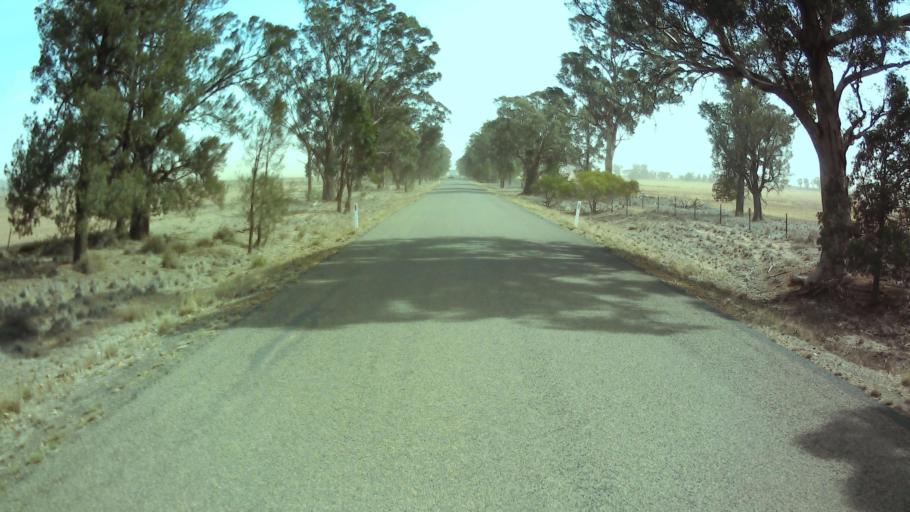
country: AU
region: New South Wales
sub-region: Weddin
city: Grenfell
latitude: -33.7616
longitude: 147.9892
